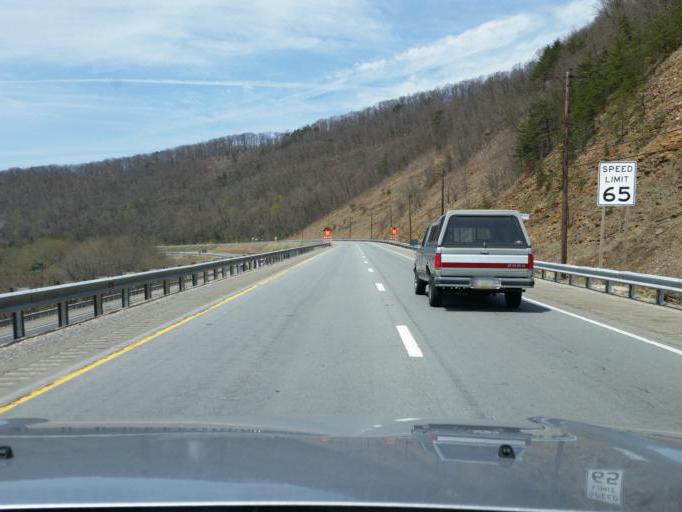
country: US
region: Pennsylvania
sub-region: Perry County
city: Newport
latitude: 40.5623
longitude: -77.1671
